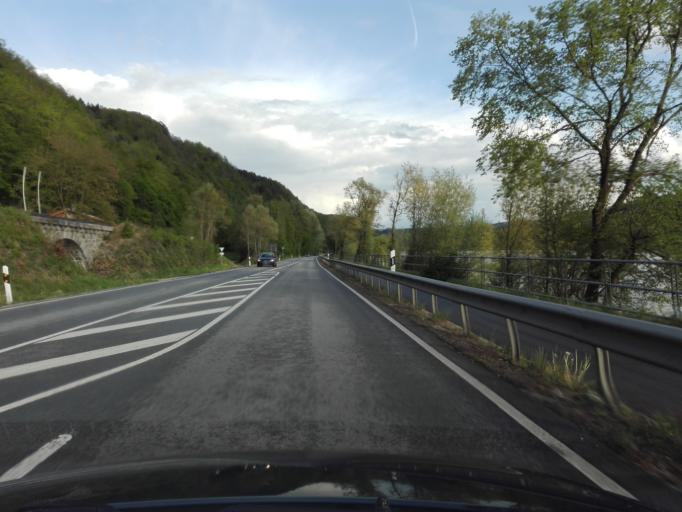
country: DE
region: Bavaria
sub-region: Lower Bavaria
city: Thyrnau
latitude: 48.5879
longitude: 13.5273
